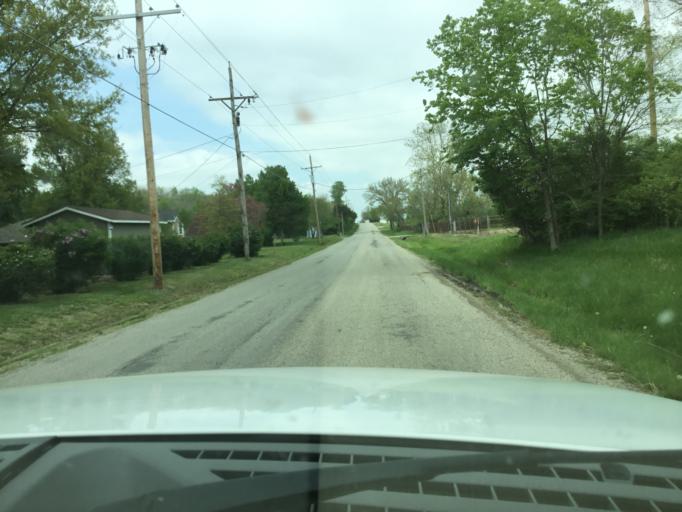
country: US
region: Kansas
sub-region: Shawnee County
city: Topeka
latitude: 39.0209
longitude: -95.5859
